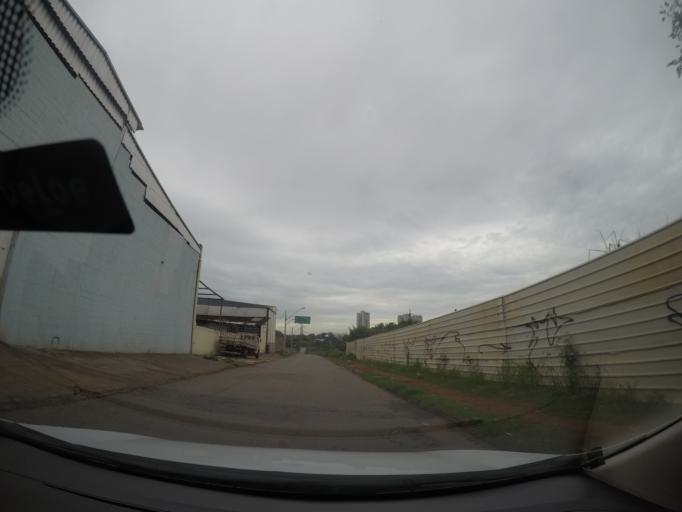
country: BR
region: Goias
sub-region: Goiania
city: Goiania
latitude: -16.6521
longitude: -49.2633
